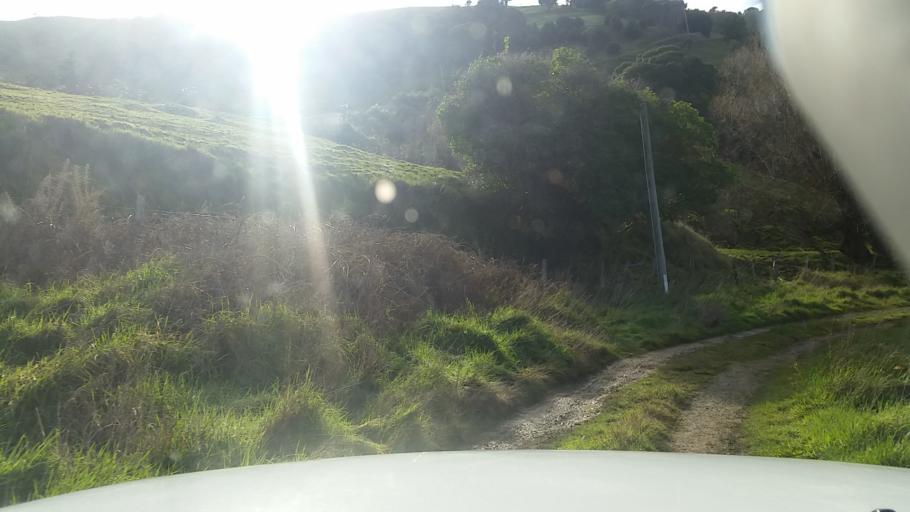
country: NZ
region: Canterbury
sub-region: Christchurch City
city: Christchurch
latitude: -43.7794
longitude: 172.9677
